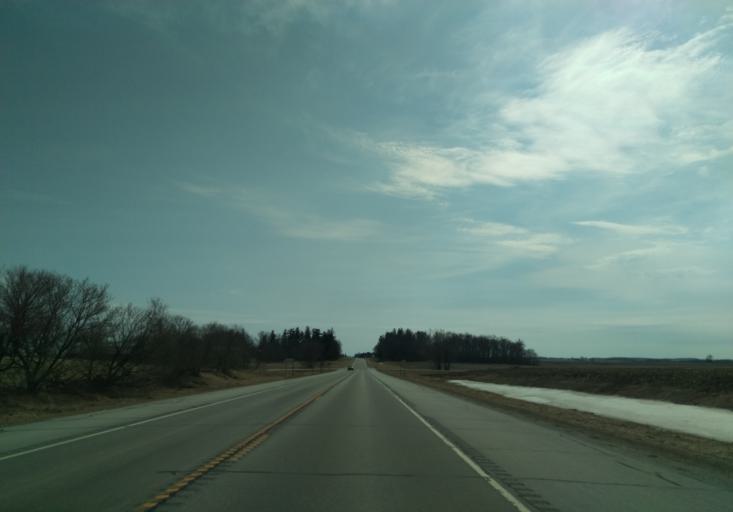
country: US
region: Minnesota
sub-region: Fillmore County
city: Harmony
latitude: 43.5031
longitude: -91.8712
